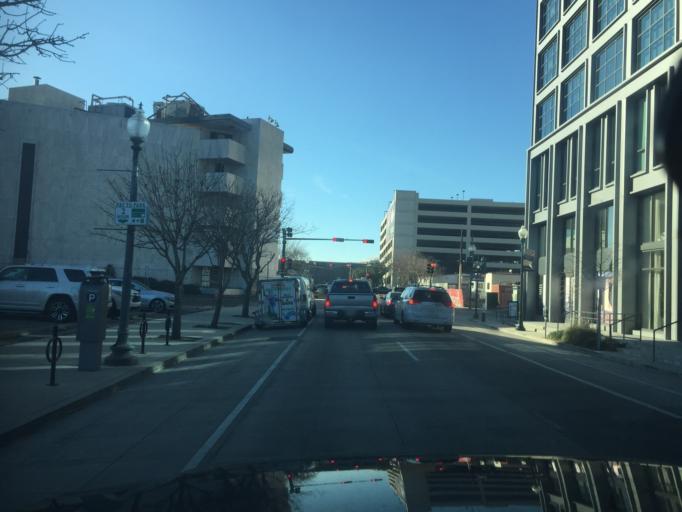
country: US
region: Louisiana
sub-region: Orleans Parish
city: New Orleans
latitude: 29.9468
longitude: -90.0756
